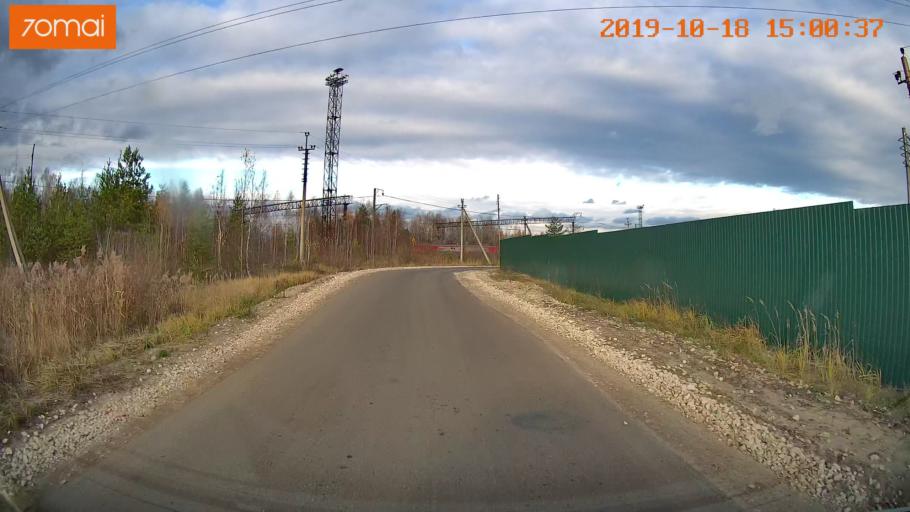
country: RU
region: Vladimir
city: Kurlovo
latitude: 55.4996
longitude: 40.5878
